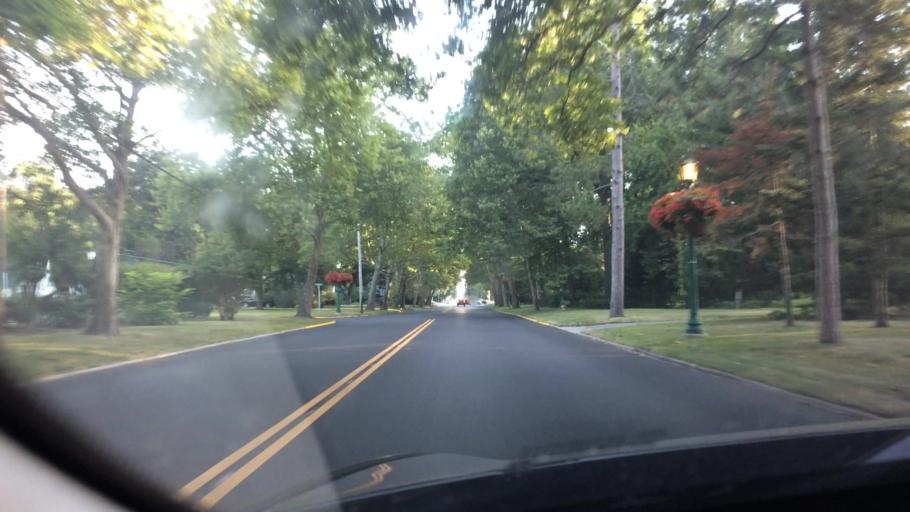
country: US
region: Ohio
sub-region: Lucas County
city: Ottawa Hills
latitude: 41.6745
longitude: -83.6439
